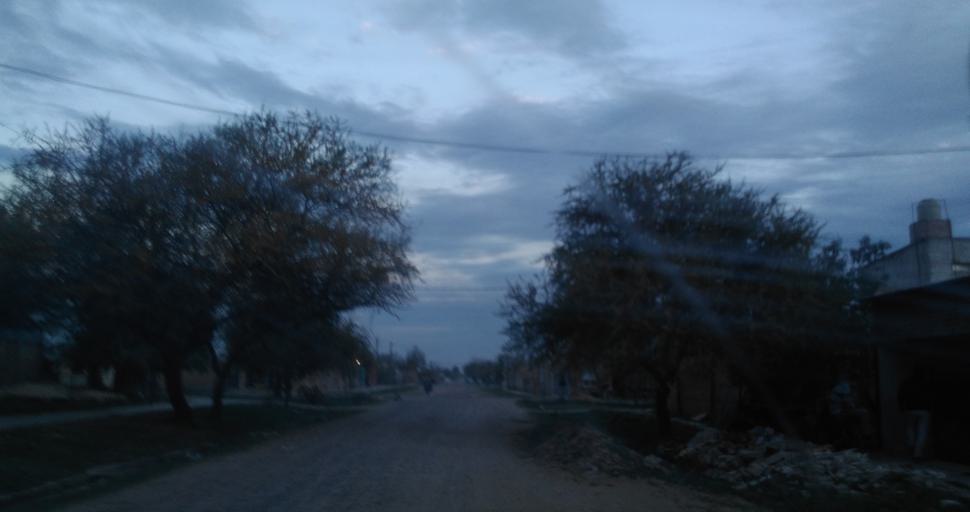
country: AR
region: Chaco
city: Resistencia
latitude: -27.4813
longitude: -59.0066
